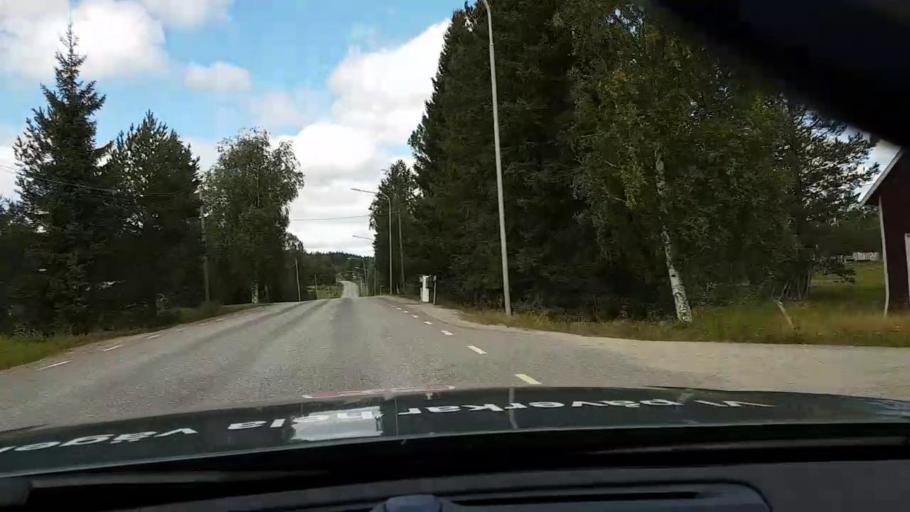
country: SE
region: Vaesternorrland
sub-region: OErnskoeldsviks Kommun
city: Bredbyn
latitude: 63.4847
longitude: 18.0874
